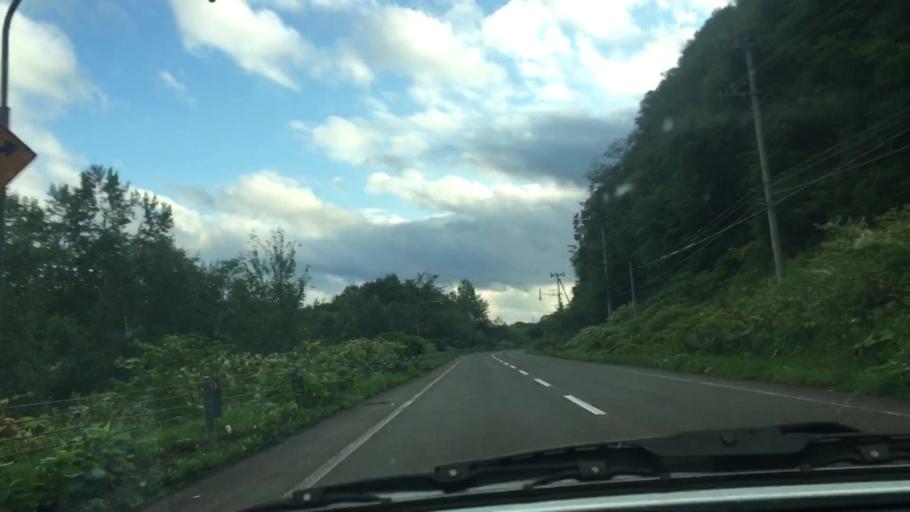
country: JP
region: Hokkaido
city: Shimo-furano
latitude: 43.0177
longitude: 142.4297
